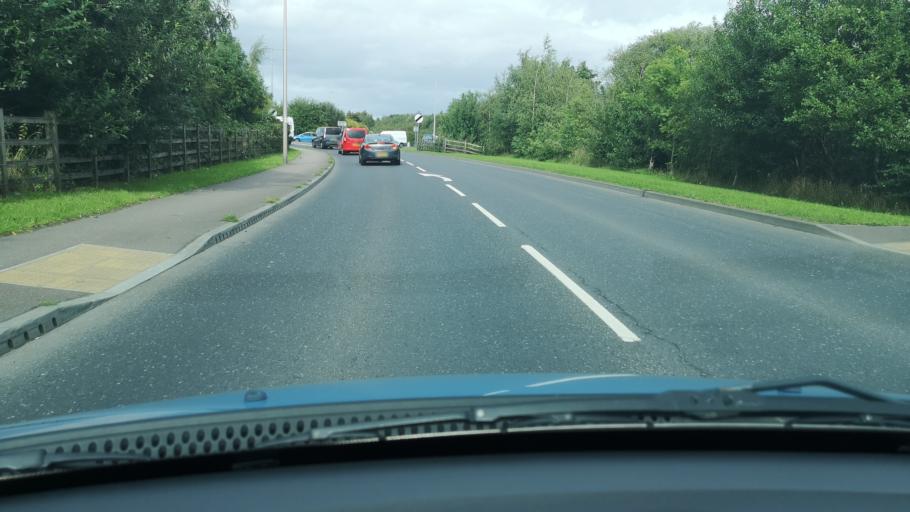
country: GB
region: England
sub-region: Barnsley
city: Cudworth
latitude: 53.5717
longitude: -1.4285
